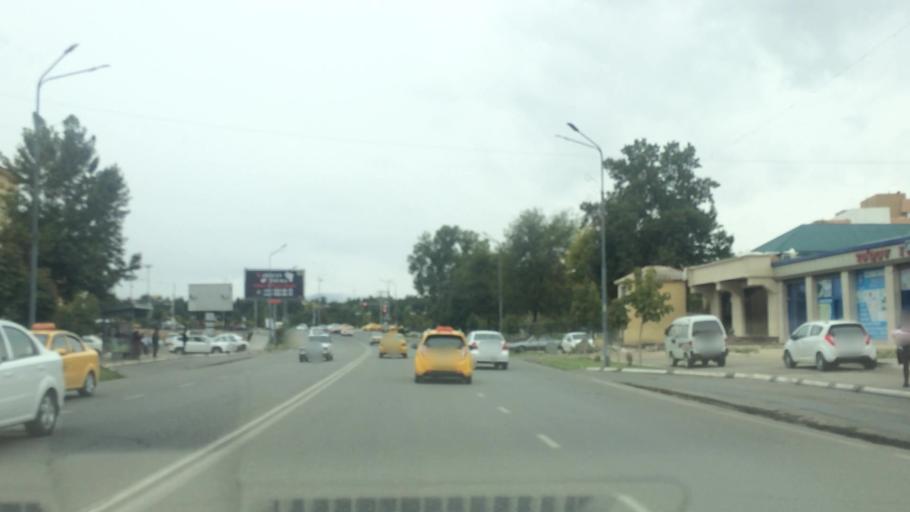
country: UZ
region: Samarqand
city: Samarqand
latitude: 39.6539
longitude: 66.9705
